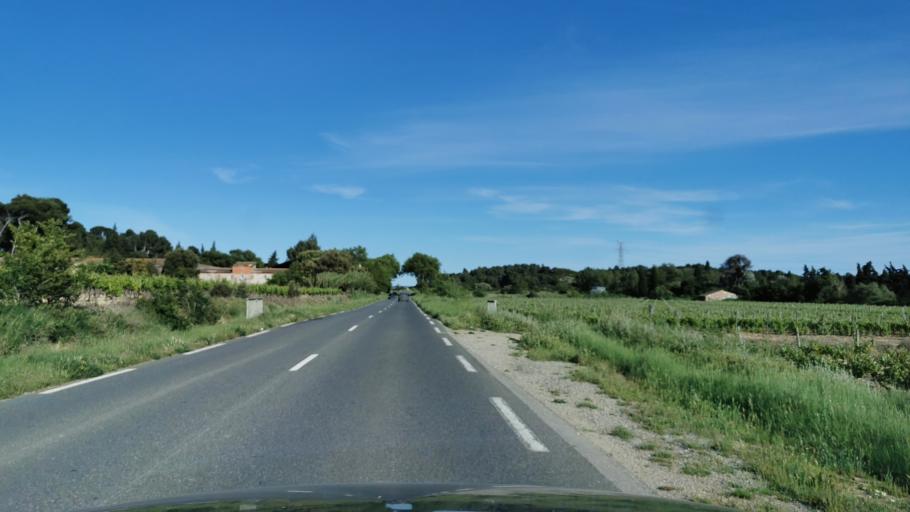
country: FR
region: Languedoc-Roussillon
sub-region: Departement de l'Aude
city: Moussan
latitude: 43.2082
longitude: 2.9518
